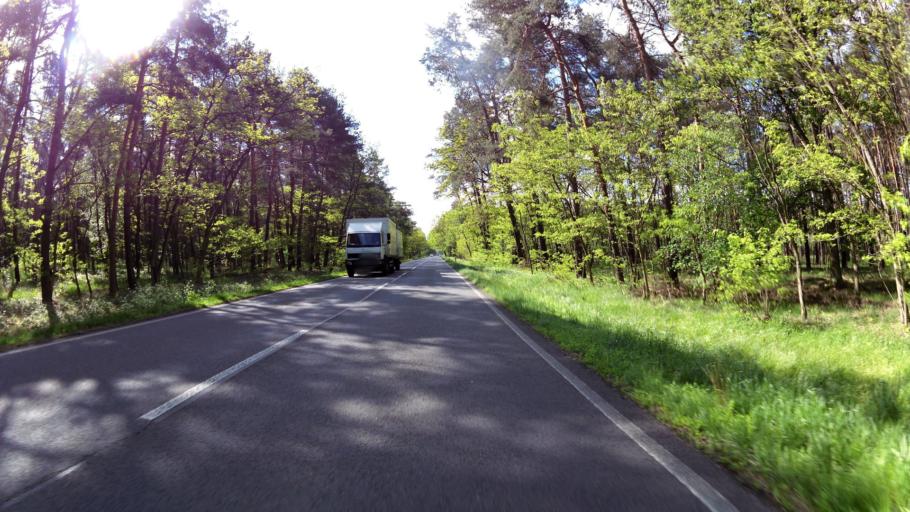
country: DE
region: Saxony-Anhalt
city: Holzdorf
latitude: 51.8624
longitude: 13.1460
